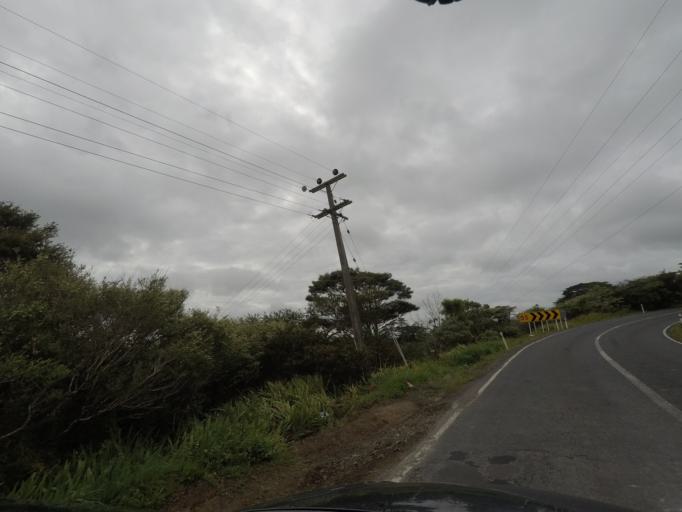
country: NZ
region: Auckland
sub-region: Auckland
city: Rosebank
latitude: -36.8113
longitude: 174.5778
